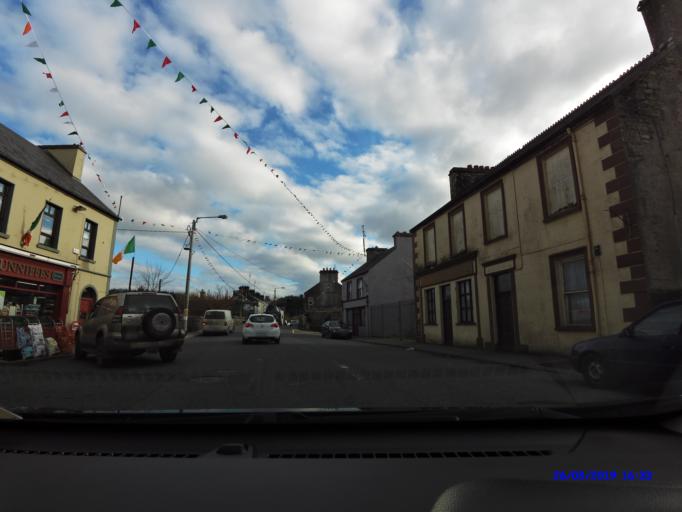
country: IE
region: Connaught
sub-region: Maigh Eo
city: Swinford
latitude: 53.8708
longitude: -8.8505
